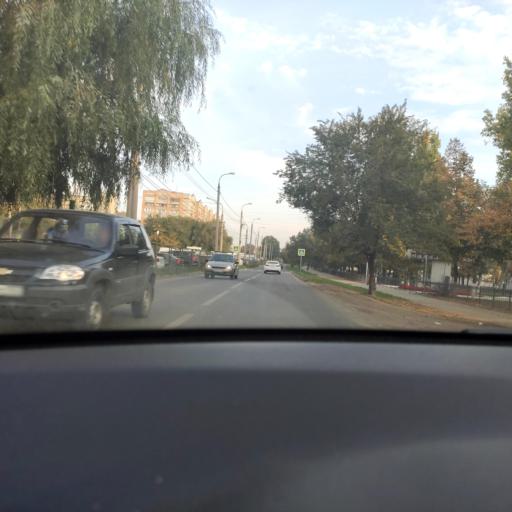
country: RU
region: Samara
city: Samara
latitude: 53.1933
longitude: 50.2002
